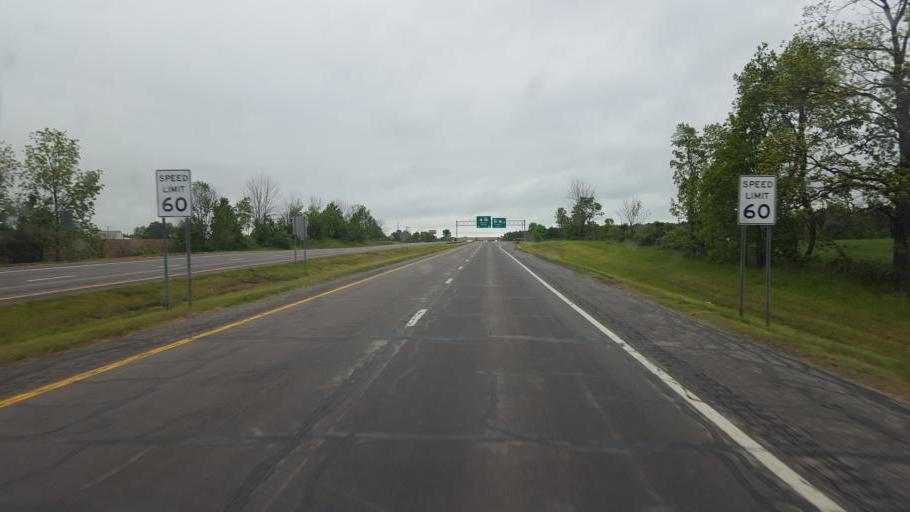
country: US
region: Ohio
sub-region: Medina County
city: Lodi
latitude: 41.0222
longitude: -82.0519
